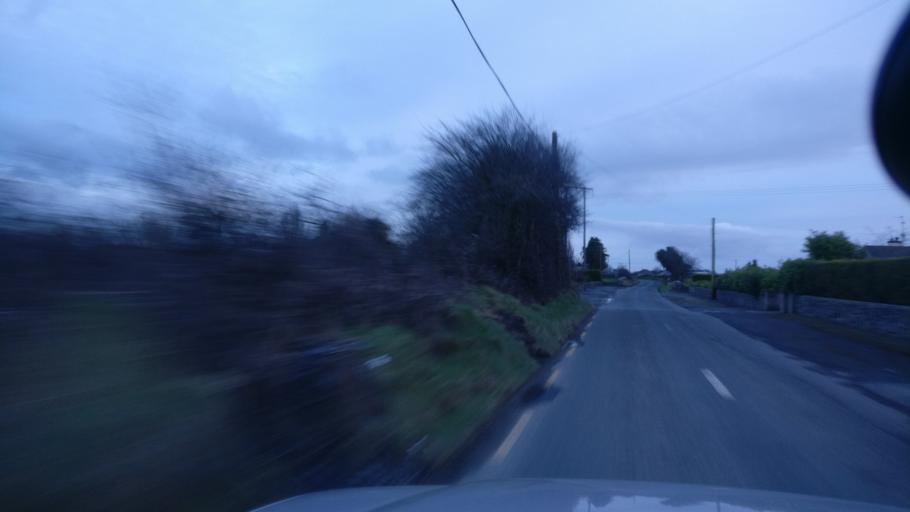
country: IE
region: Connaught
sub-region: County Galway
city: Athenry
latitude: 53.2668
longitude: -8.6904
